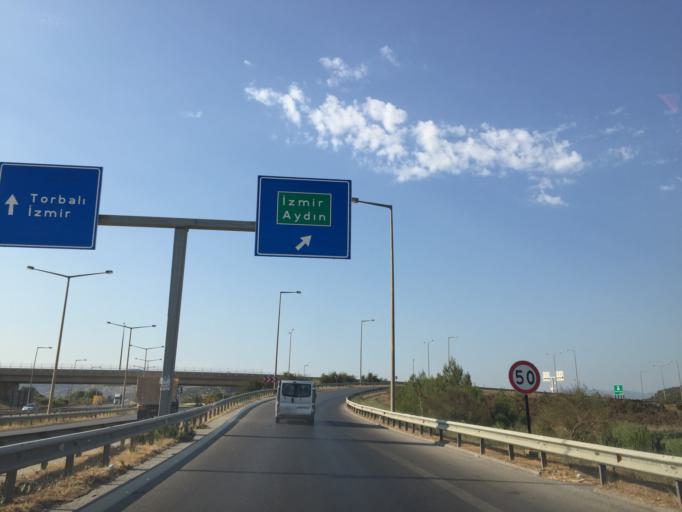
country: TR
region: Izmir
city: Belevi
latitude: 38.0299
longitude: 27.4442
